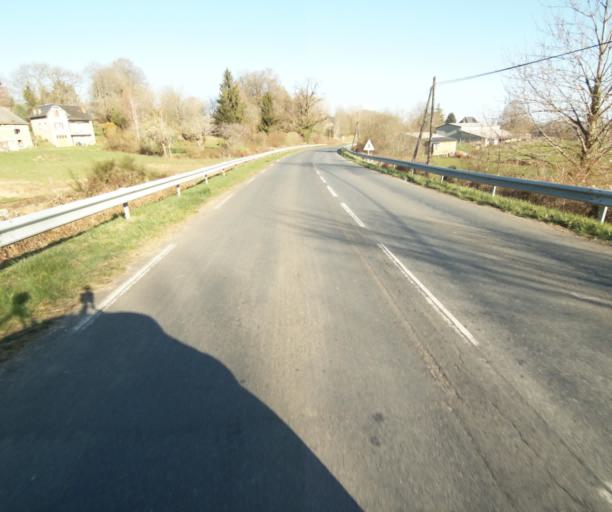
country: FR
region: Limousin
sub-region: Departement de la Correze
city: Uzerche
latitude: 45.3916
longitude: 1.5951
